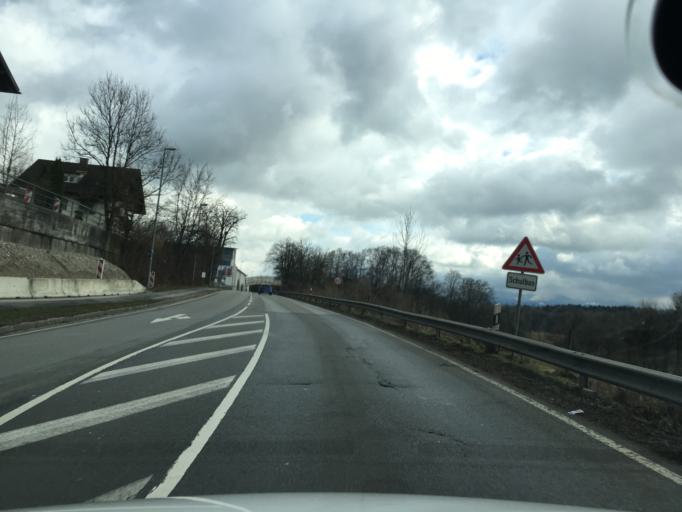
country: DE
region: Bavaria
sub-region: Upper Bavaria
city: Stephanskirchen
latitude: 47.8469
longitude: 12.1570
